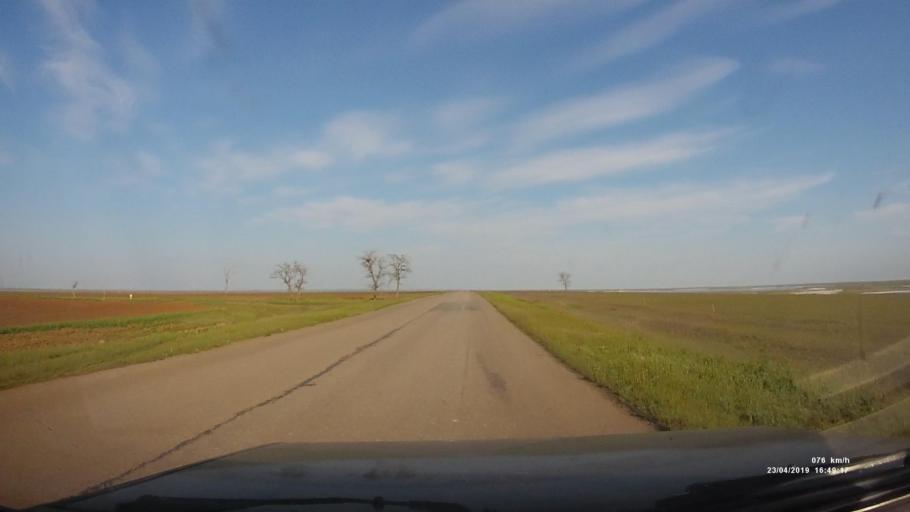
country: RU
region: Kalmykiya
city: Priyutnoye
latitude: 46.3316
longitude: 43.2743
